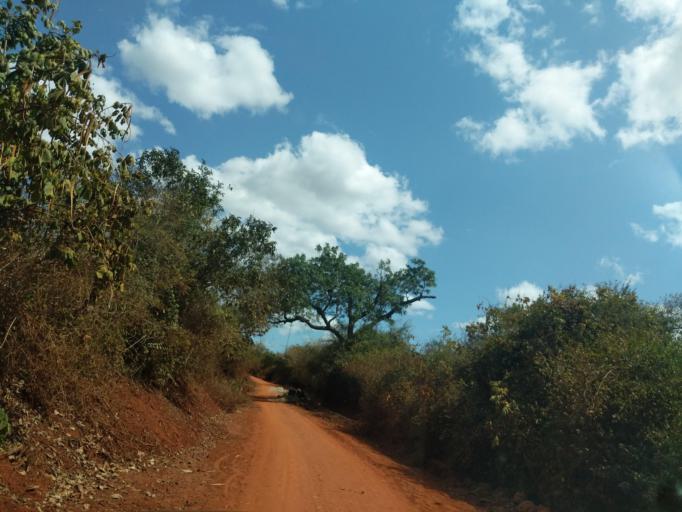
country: TZ
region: Tanga
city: Chanika
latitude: -5.5170
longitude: 38.3566
